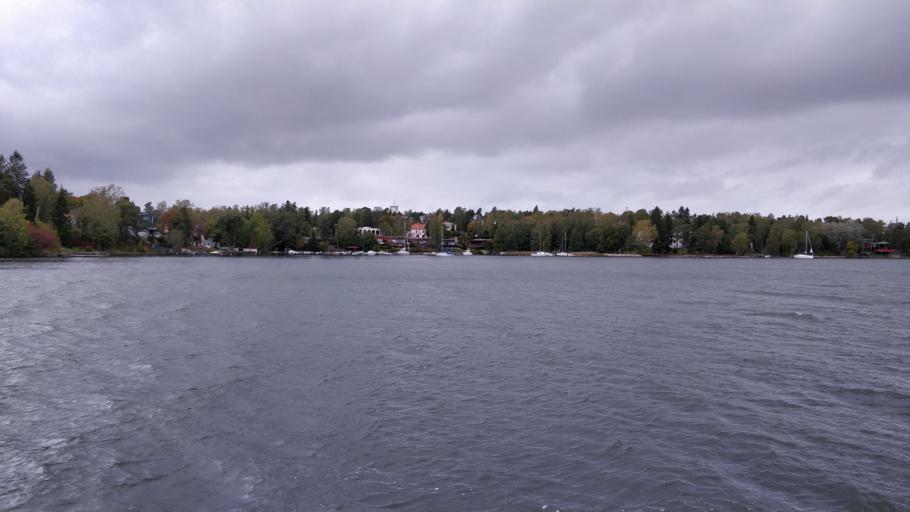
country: FI
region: Uusimaa
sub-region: Helsinki
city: Helsinki
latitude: 60.1809
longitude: 25.0218
